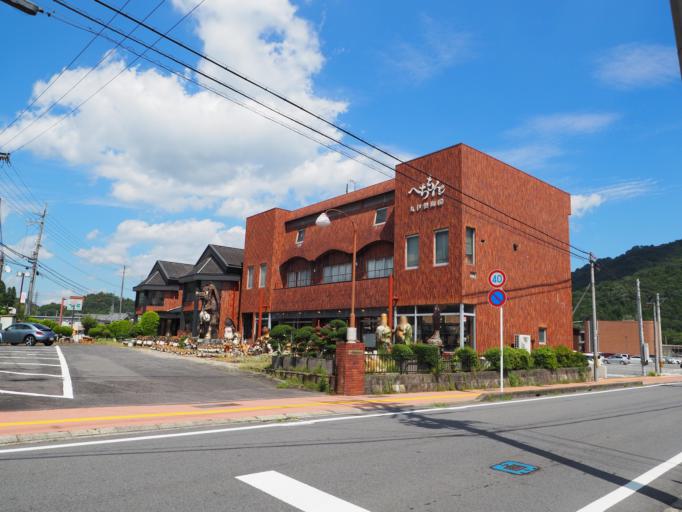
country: JP
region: Mie
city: Ueno-ebisumachi
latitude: 34.8780
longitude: 136.0573
